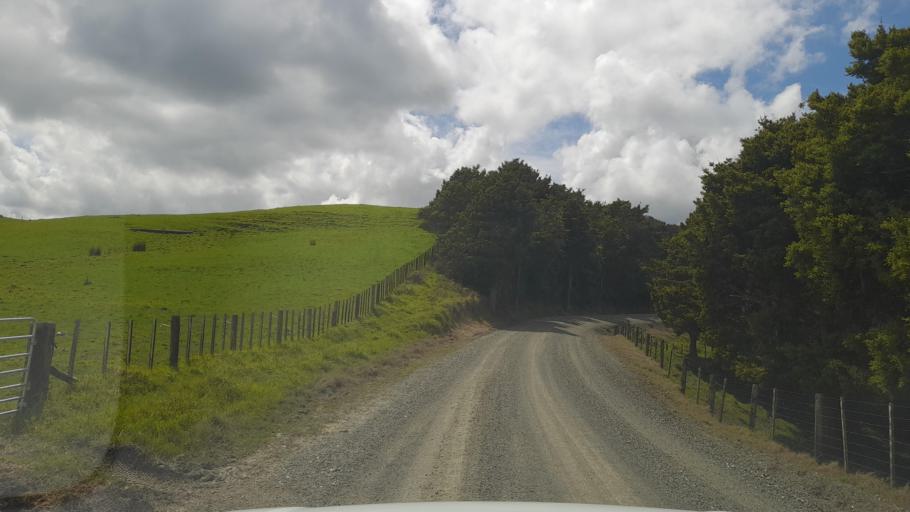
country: NZ
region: Auckland
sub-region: Auckland
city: Wellsford
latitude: -36.2115
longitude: 174.3287
